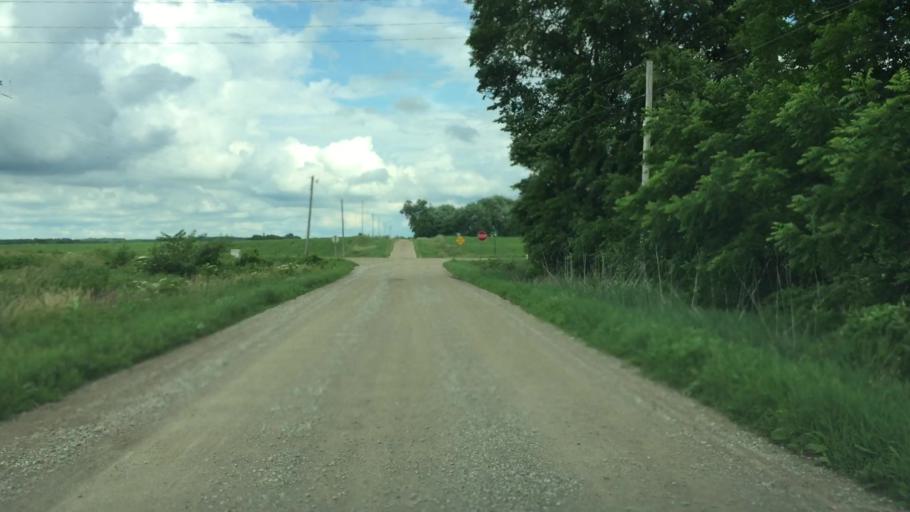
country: US
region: Iowa
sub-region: Jasper County
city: Newton
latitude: 41.7460
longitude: -93.0203
